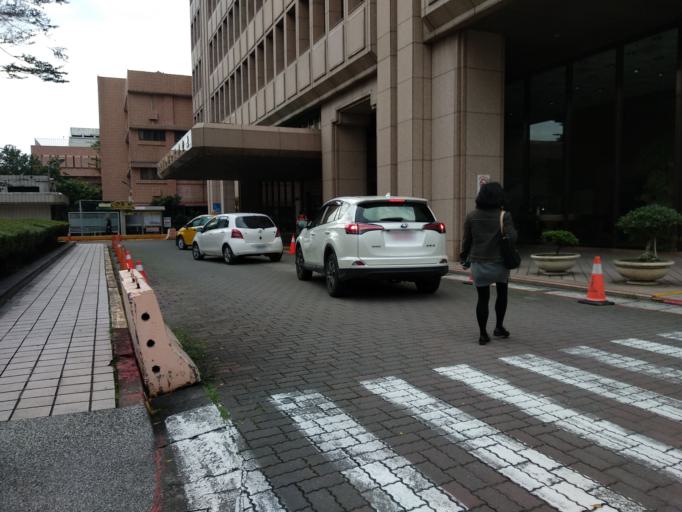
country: TW
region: Taipei
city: Taipei
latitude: 25.0428
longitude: 121.5199
